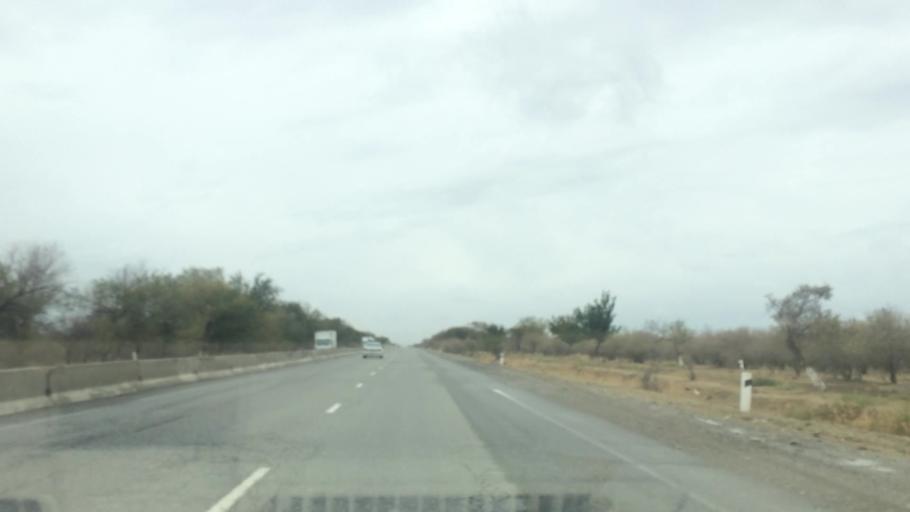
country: UZ
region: Samarqand
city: Bulung'ur
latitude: 39.8219
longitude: 67.3921
